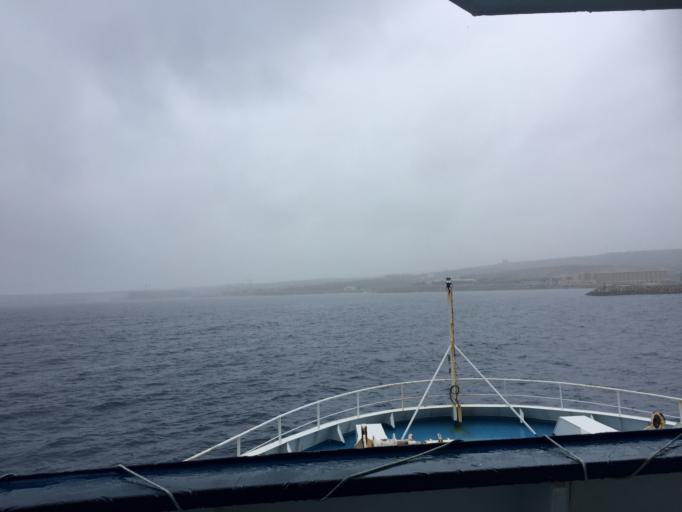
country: MT
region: Ghajnsielem
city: Mgarr
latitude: 35.9948
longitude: 14.3275
